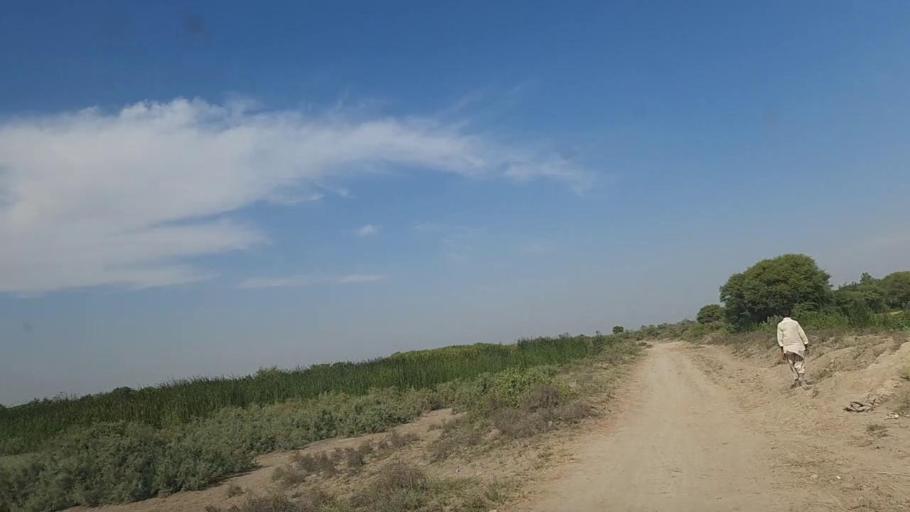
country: PK
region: Sindh
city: Mirpur Batoro
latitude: 24.7969
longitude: 68.2693
